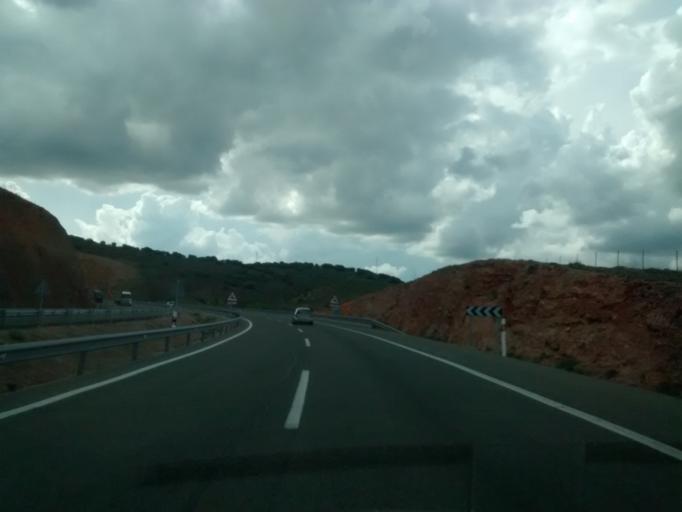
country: ES
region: Castille and Leon
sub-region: Provincia de Soria
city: Medinaceli
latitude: 41.2047
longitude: -2.3625
